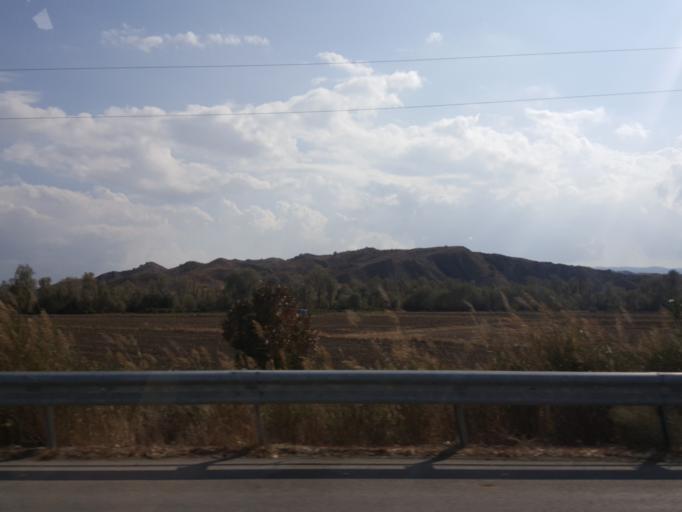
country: TR
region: Corum
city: Sungurlu
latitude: 40.1821
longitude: 34.4826
